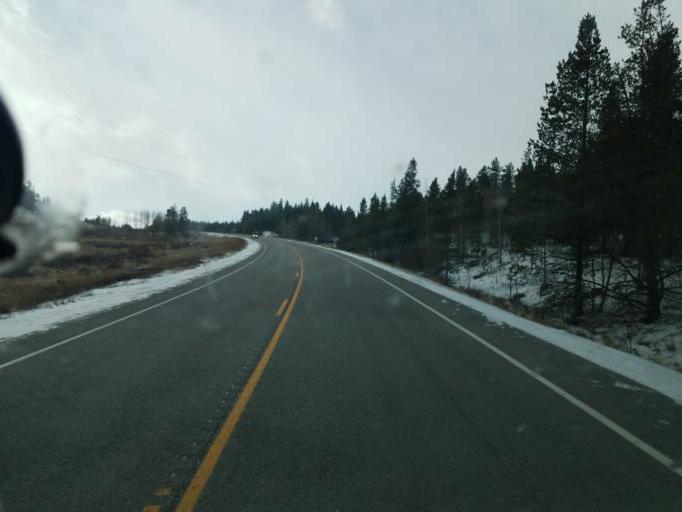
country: US
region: Colorado
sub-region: Summit County
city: Breckenridge
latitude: 39.4211
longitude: -105.7650
